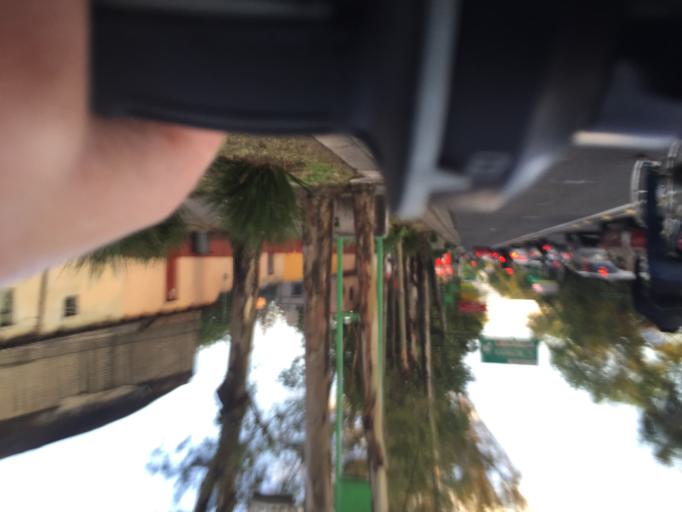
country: MX
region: Mexico City
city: Colonia Nativitas
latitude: 19.3779
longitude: -99.1484
